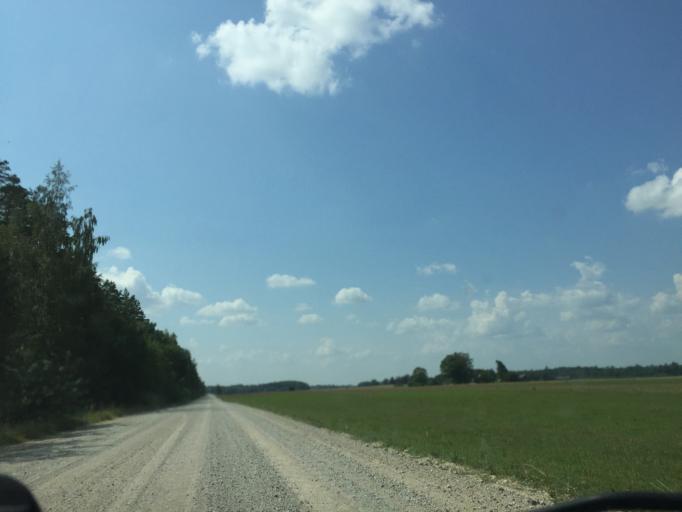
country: LT
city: Zagare
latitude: 56.3823
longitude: 23.2933
